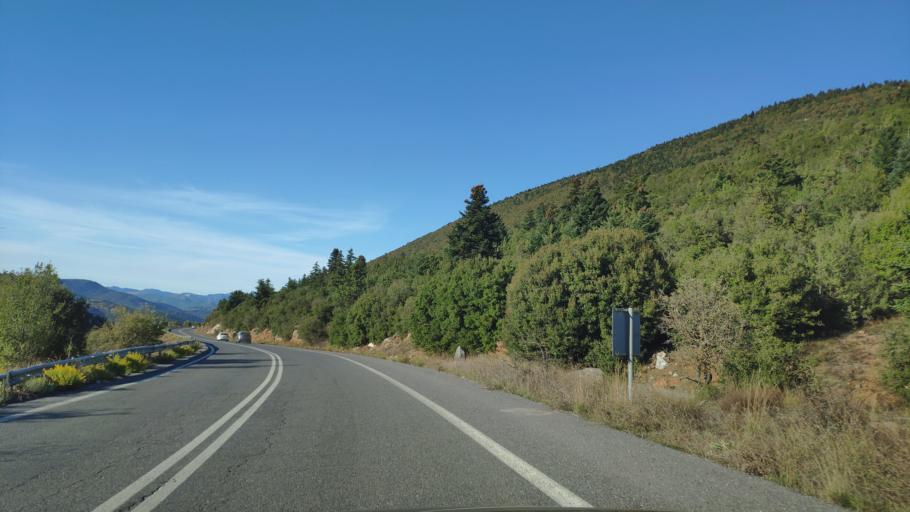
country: GR
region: Peloponnese
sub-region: Nomos Arkadias
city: Langadhia
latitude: 37.6980
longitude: 22.1992
